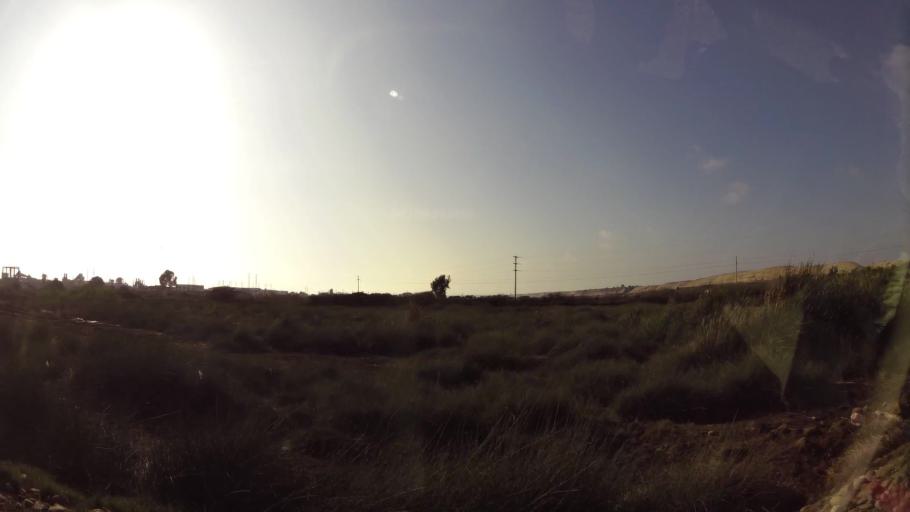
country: PE
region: Ica
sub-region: Provincia de Chincha
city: Chincha Baja
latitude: -13.4514
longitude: -76.1809
